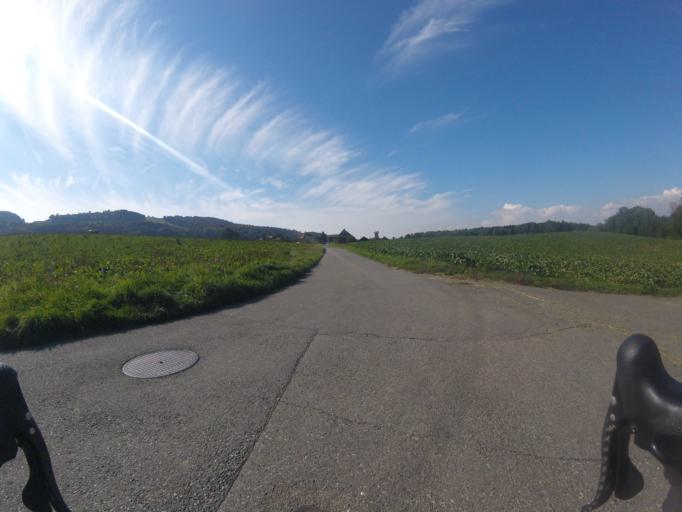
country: CH
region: Bern
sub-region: Bern-Mittelland District
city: Kehrsatz
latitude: 46.9215
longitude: 7.4725
